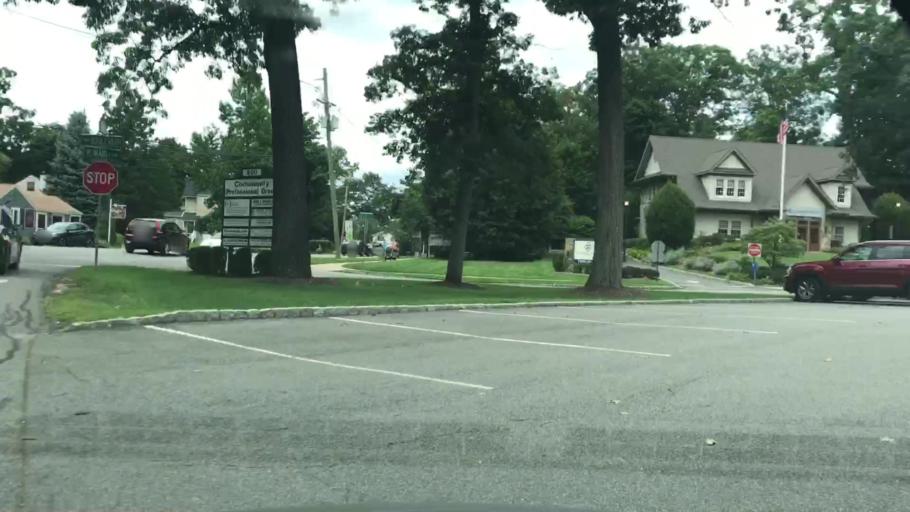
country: US
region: New Jersey
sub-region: Morris County
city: Mountain Lakes
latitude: 40.9038
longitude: -74.4253
